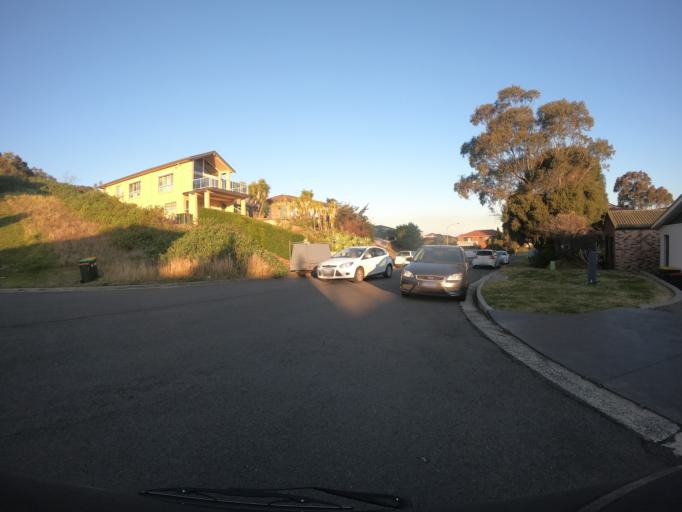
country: AU
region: New South Wales
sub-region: Wollongong
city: Berkeley
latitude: -34.4753
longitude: 150.8599
